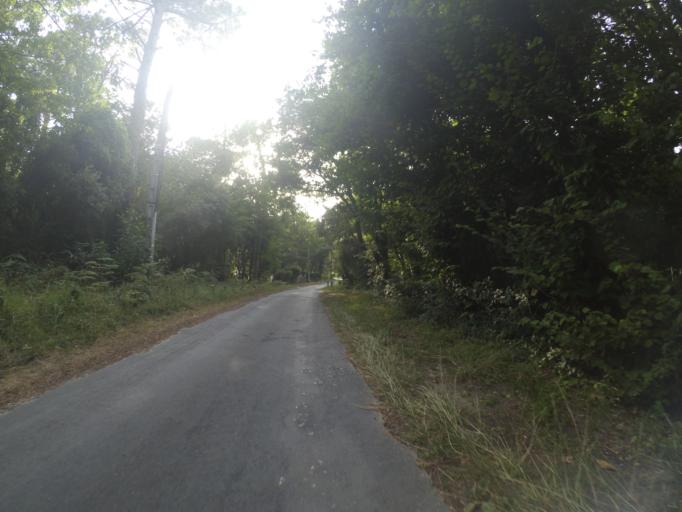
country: FR
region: Poitou-Charentes
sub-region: Departement de la Charente-Maritime
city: Meschers-sur-Gironde
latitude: 45.5789
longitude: -0.9768
